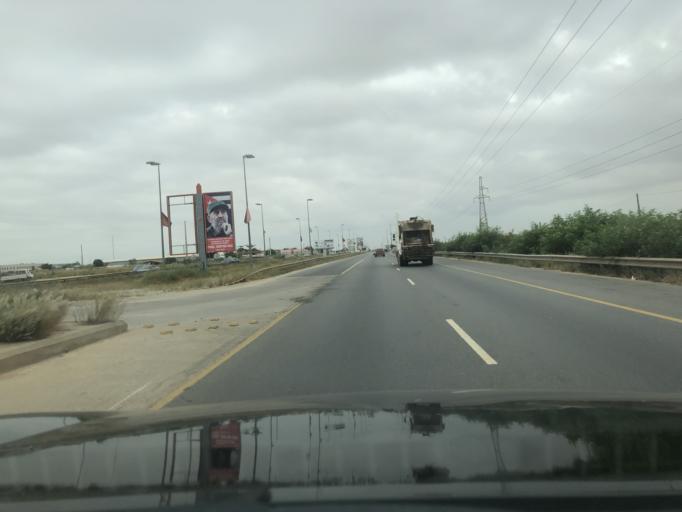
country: AO
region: Luanda
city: Luanda
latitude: -8.9733
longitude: 13.2447
